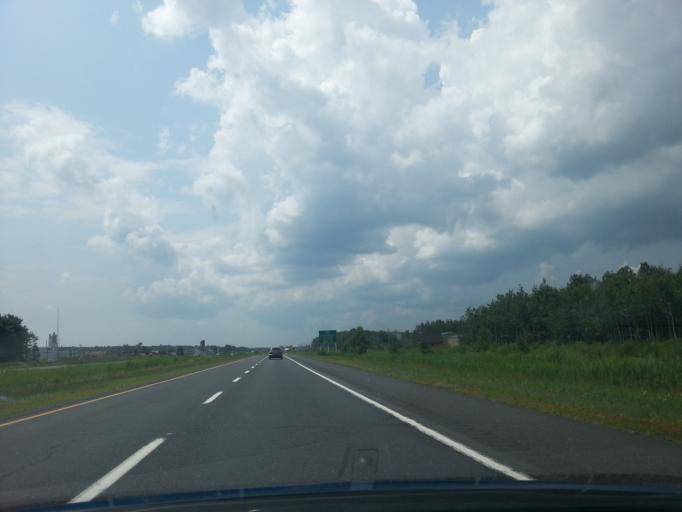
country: CA
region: Quebec
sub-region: Chaudiere-Appalaches
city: Saint-Antoine-de-Tilly
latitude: 46.5512
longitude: -71.6026
